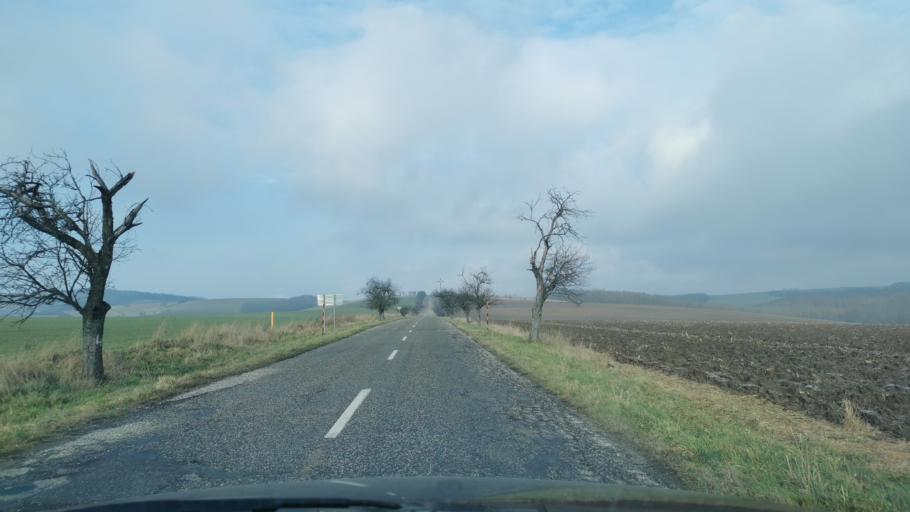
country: SK
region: Trnavsky
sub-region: Okres Senica
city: Senica
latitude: 48.7184
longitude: 17.3226
